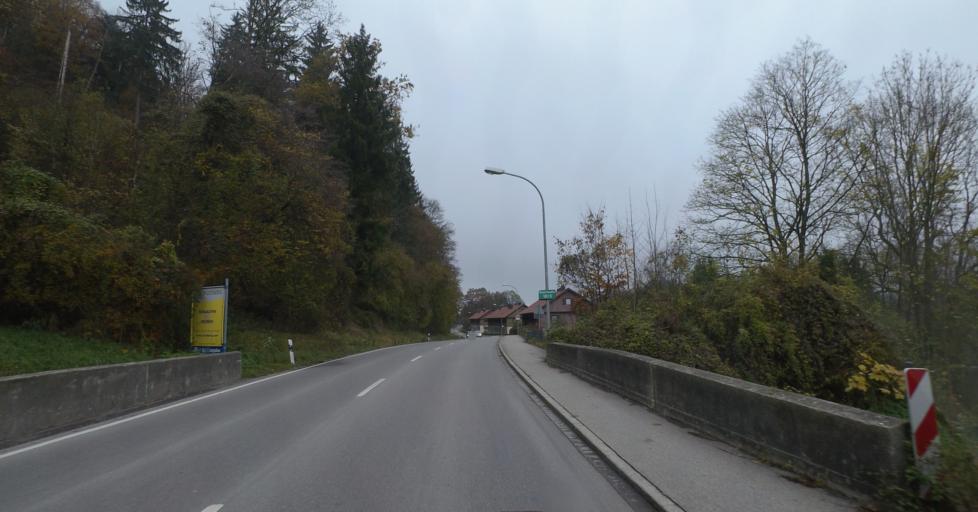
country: DE
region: Bavaria
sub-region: Upper Bavaria
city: Trostberg an der Alz
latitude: 48.0375
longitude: 12.5604
